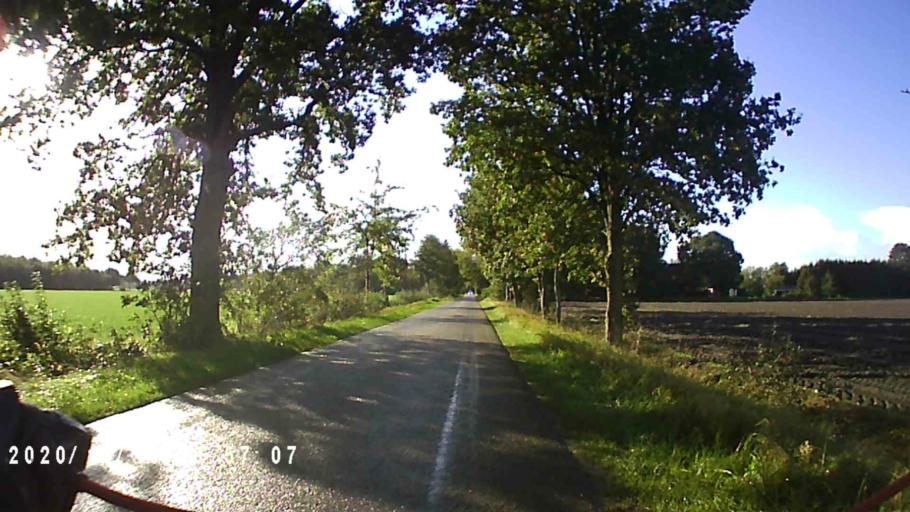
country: NL
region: Friesland
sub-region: Gemeente Achtkarspelen
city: Surhuisterveen
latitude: 53.1493
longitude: 6.2065
